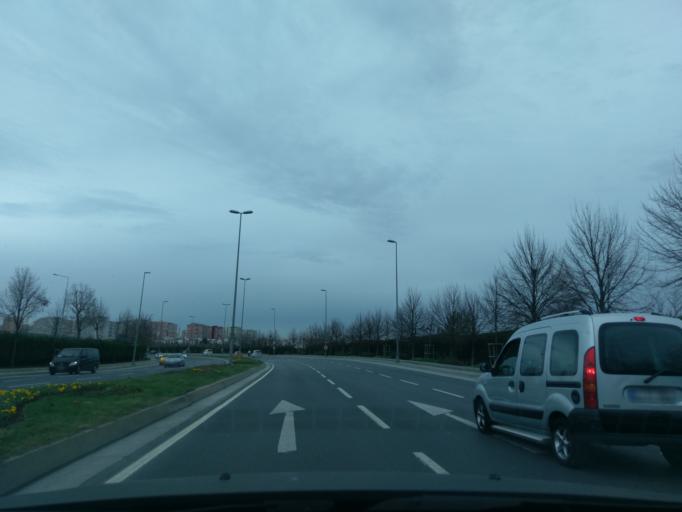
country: TR
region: Istanbul
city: Bahcelievler
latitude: 40.9777
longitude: 28.8398
